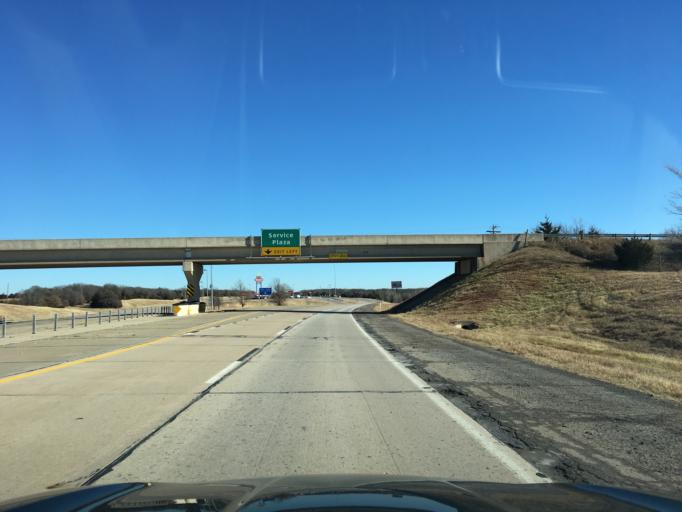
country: US
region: Oklahoma
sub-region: Pawnee County
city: Pawnee
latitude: 36.2247
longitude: -96.8032
